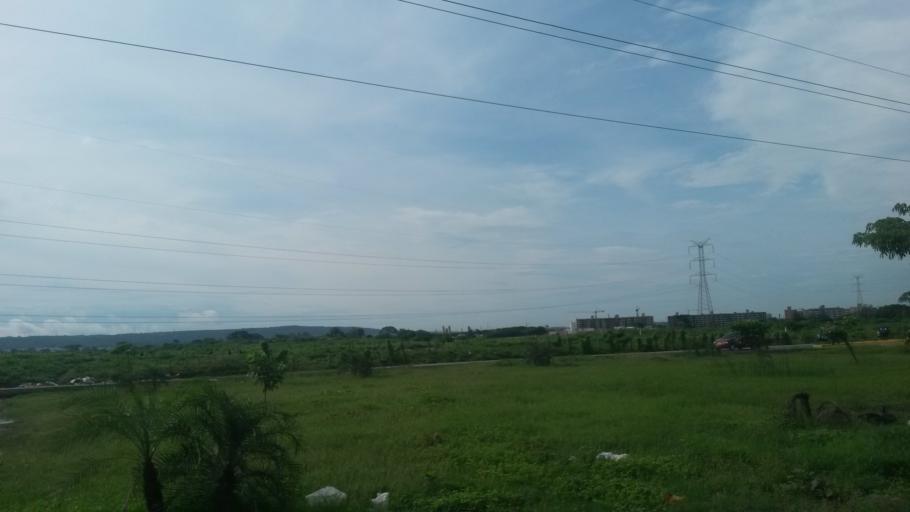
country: CO
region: Bolivar
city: Cartagena
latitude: 10.4056
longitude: -75.4538
